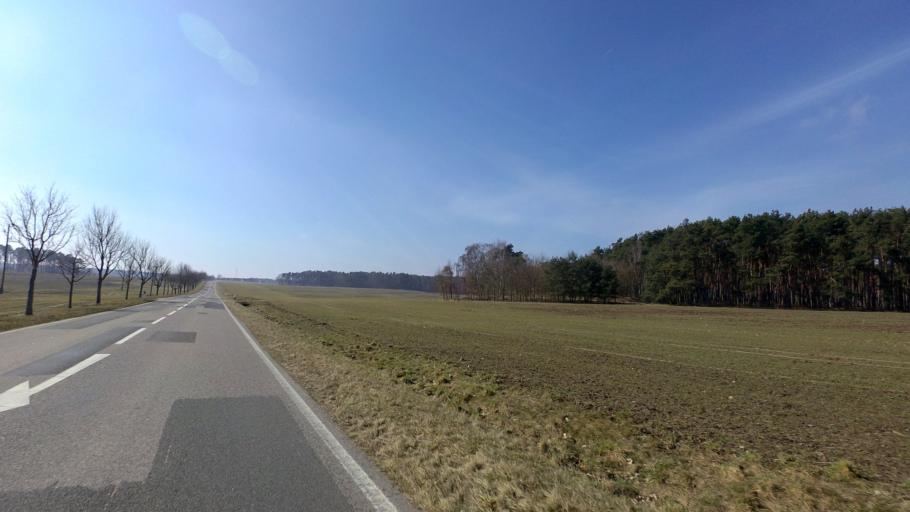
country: DE
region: Brandenburg
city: Wiesenburg
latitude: 52.0661
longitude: 12.5105
